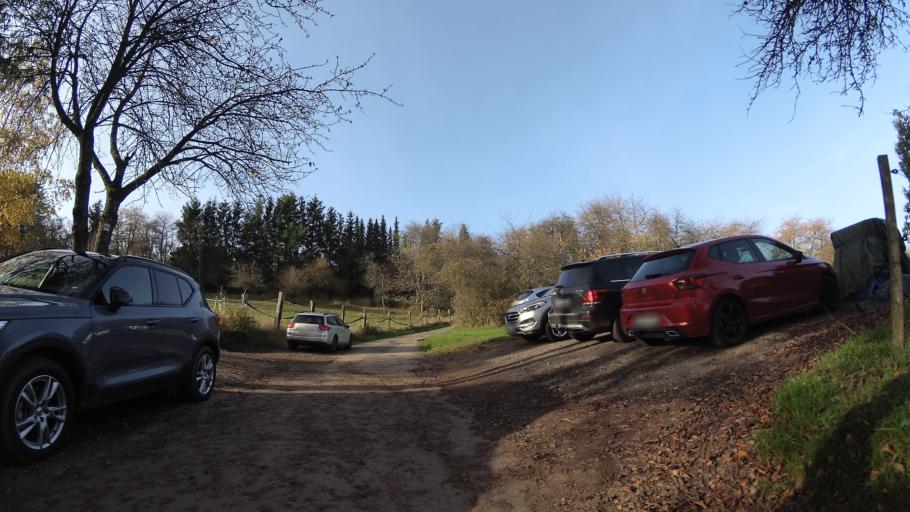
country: DE
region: Saarland
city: Hangard
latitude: 49.3846
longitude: 7.2004
